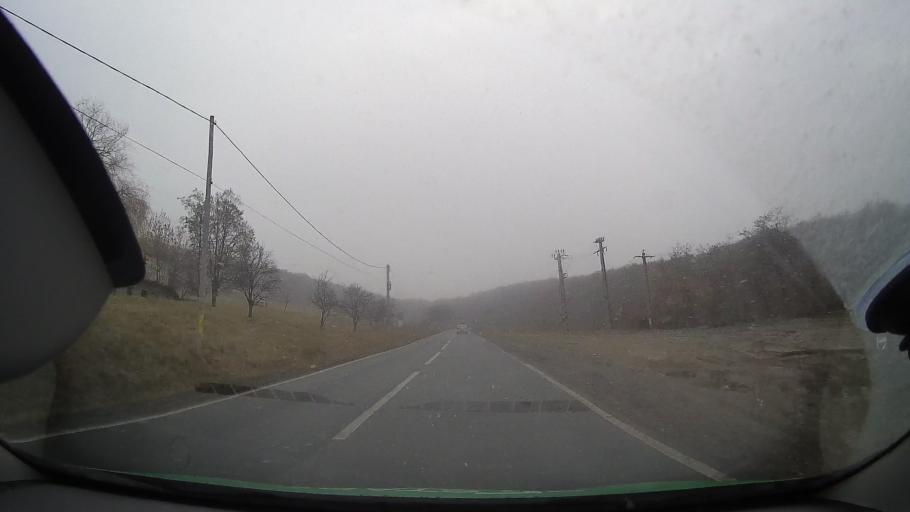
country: RO
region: Sibiu
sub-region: Comuna Blajel
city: Blajel
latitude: 46.1932
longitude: 24.3243
